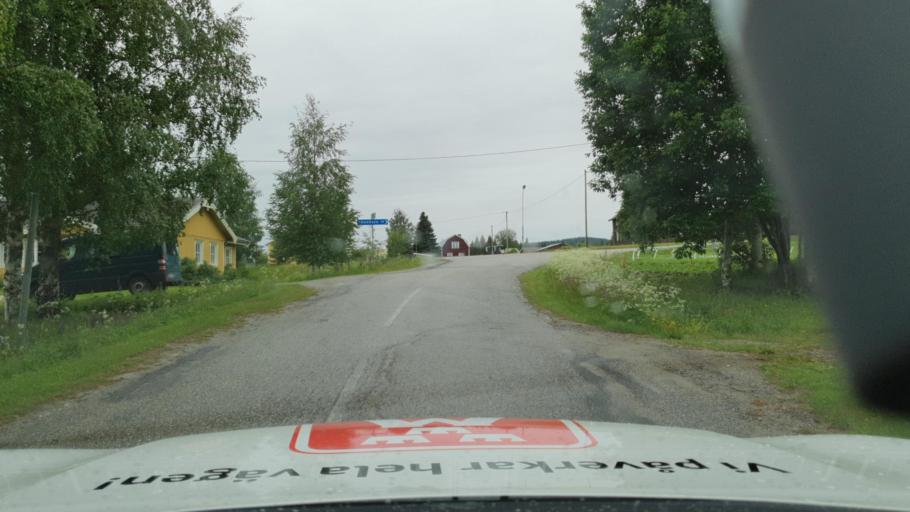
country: SE
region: Vaesterbotten
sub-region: Asele Kommun
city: Asele
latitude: 63.9656
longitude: 17.1071
